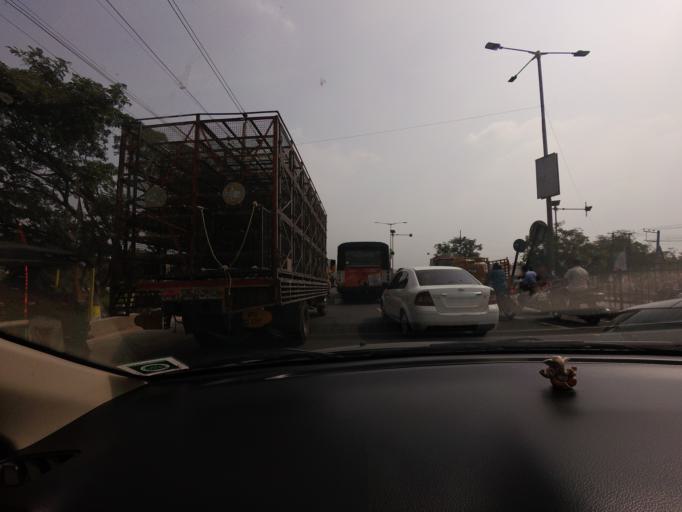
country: IN
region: Andhra Pradesh
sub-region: Krishna
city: Vijayawada
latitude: 16.4973
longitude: 80.6416
